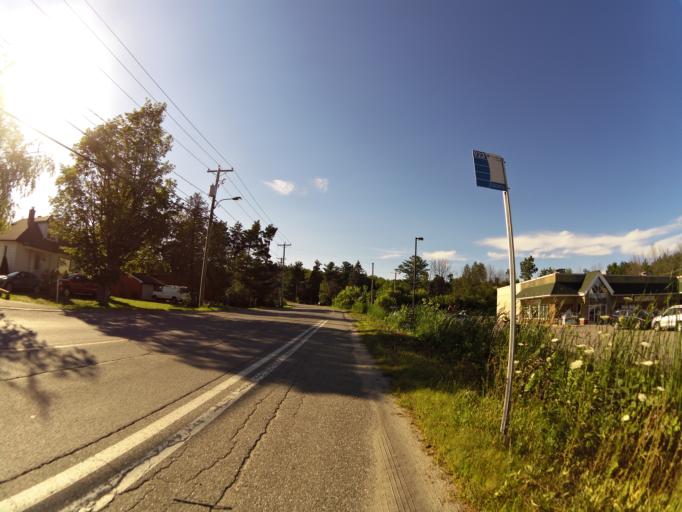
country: CA
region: Quebec
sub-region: Outaouais
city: Gatineau
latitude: 45.5079
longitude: -75.7859
